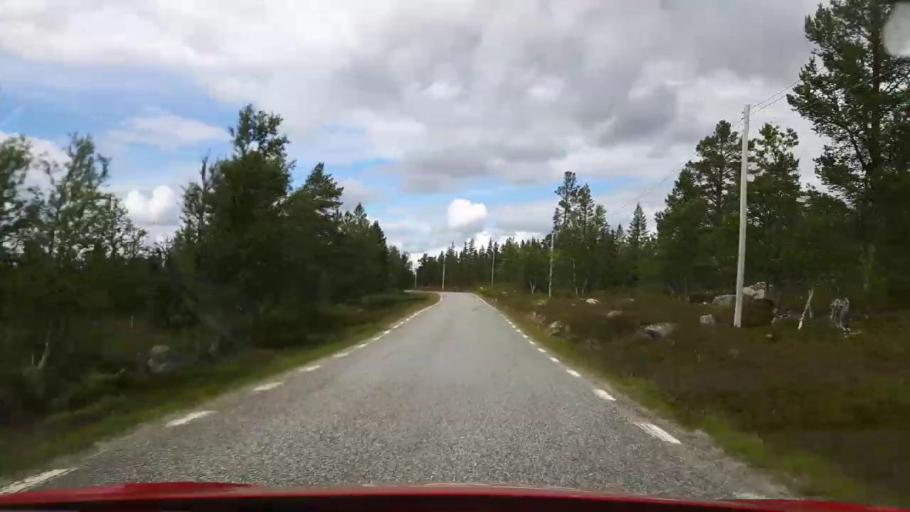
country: NO
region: Hedmark
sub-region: Engerdal
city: Engerdal
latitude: 62.3311
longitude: 12.8069
